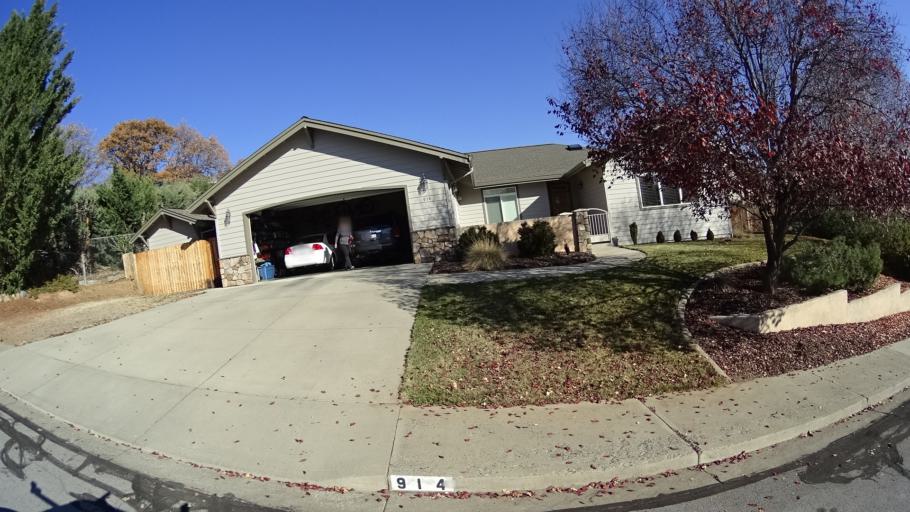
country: US
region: California
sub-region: Siskiyou County
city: Yreka
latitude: 41.7436
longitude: -122.6459
